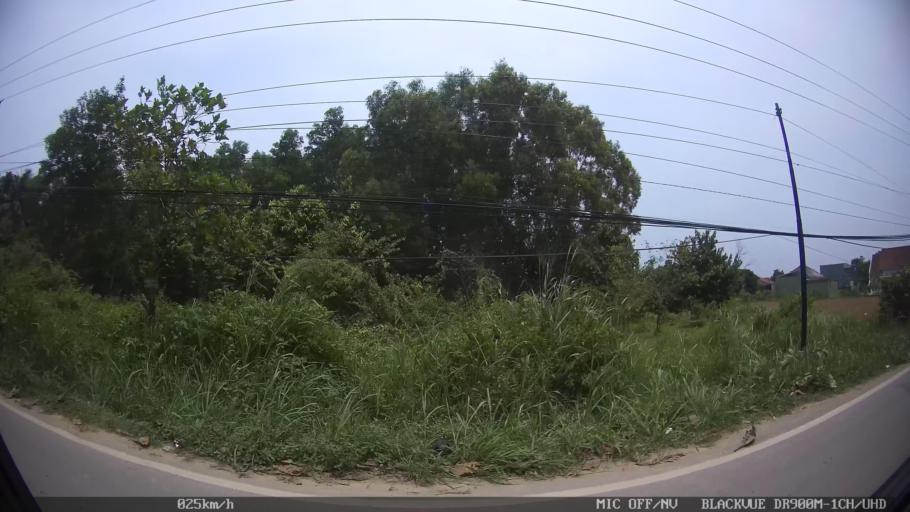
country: ID
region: Lampung
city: Kedaton
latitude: -5.4020
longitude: 105.3162
